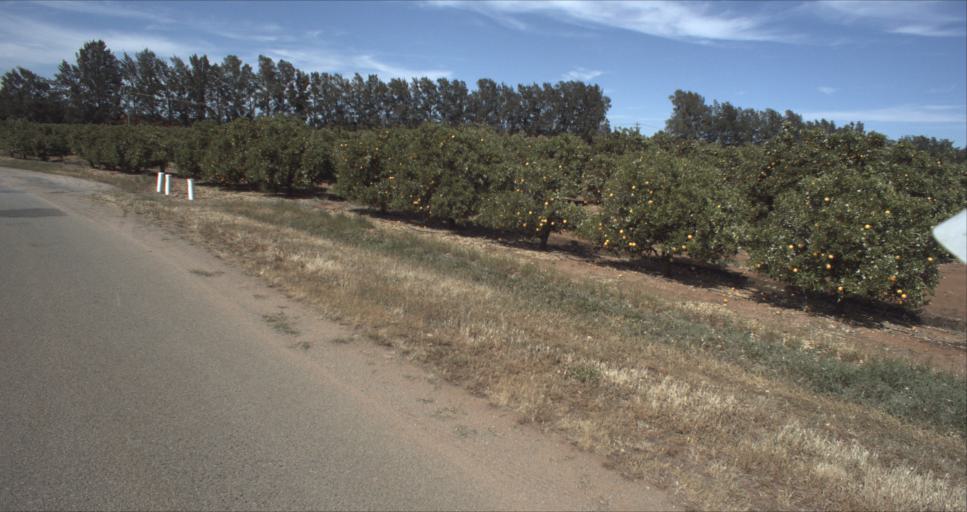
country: AU
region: New South Wales
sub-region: Leeton
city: Leeton
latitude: -34.5901
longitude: 146.4624
